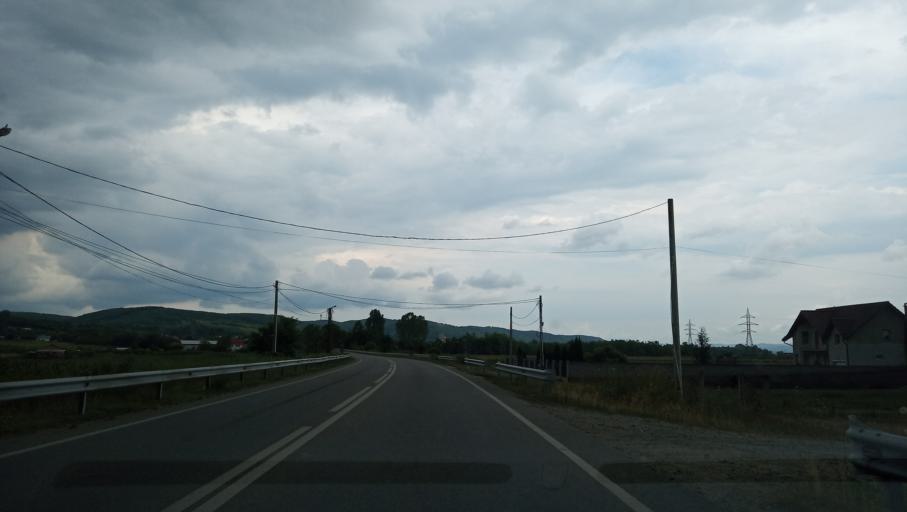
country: RO
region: Gorj
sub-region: Oras Rovinari
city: Rovinari
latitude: 44.9005
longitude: 23.1922
